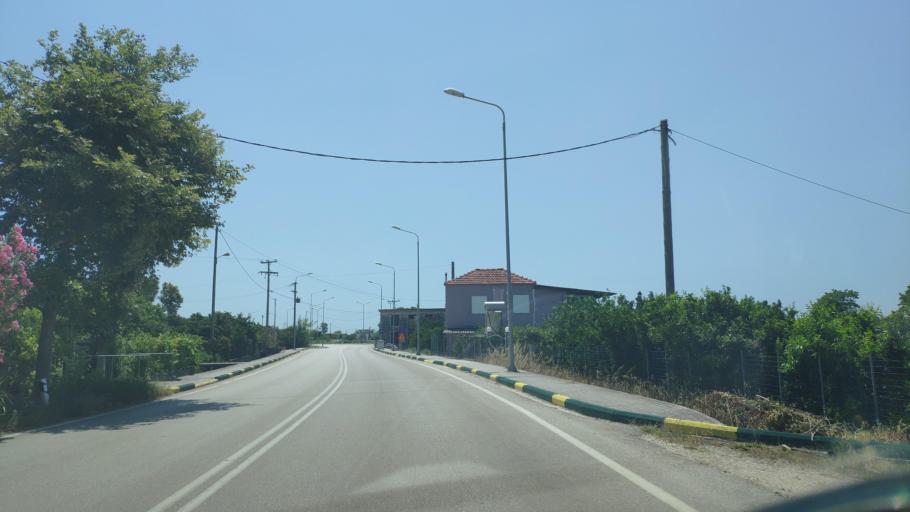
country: GR
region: Epirus
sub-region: Nomos Artas
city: Arta
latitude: 39.1424
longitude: 20.9802
